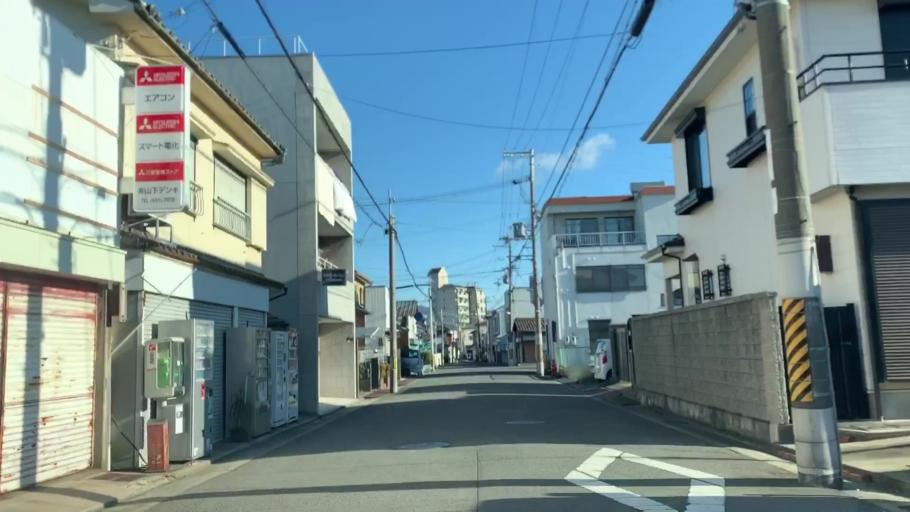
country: JP
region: Wakayama
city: Wakayama-shi
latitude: 34.2407
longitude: 135.1824
